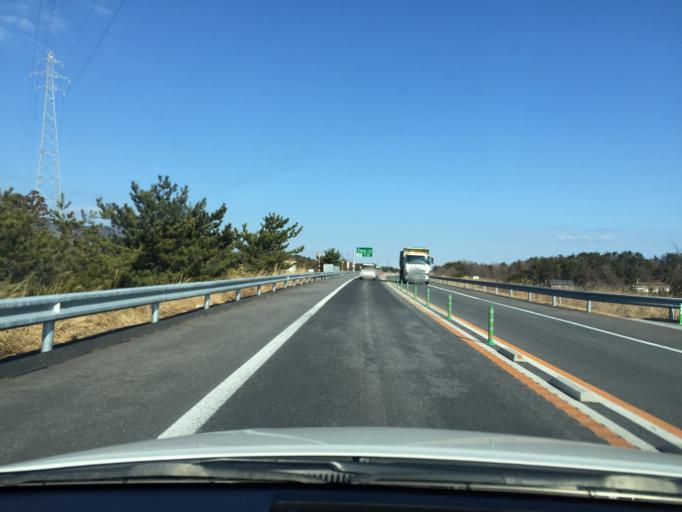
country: JP
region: Fukushima
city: Namie
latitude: 37.3707
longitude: 140.9669
